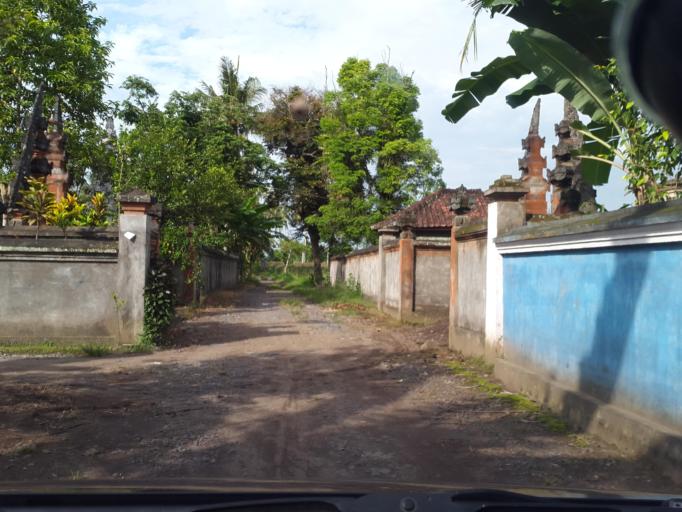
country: ID
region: West Nusa Tenggara
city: Ranggagata
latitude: -8.7015
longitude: 116.1377
